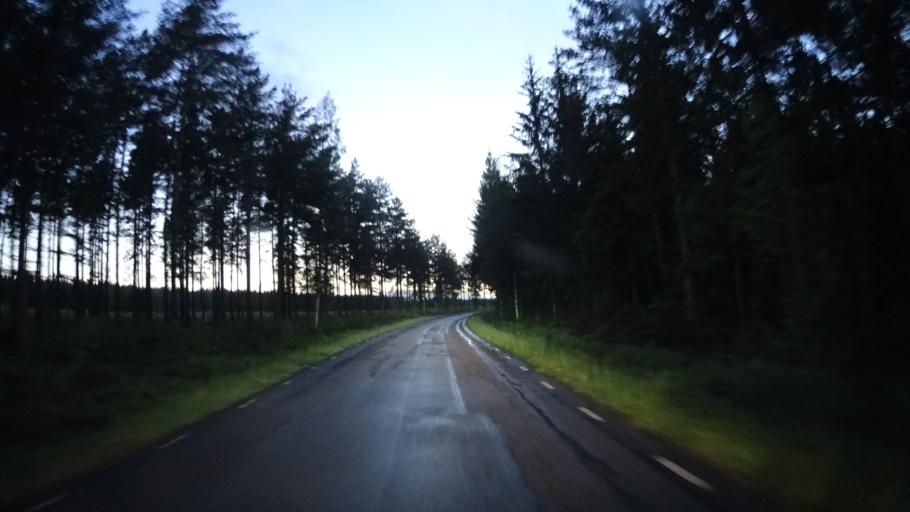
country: SE
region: Kalmar
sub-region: Vasterviks Kommun
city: Vaestervik
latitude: 57.7756
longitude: 16.5324
